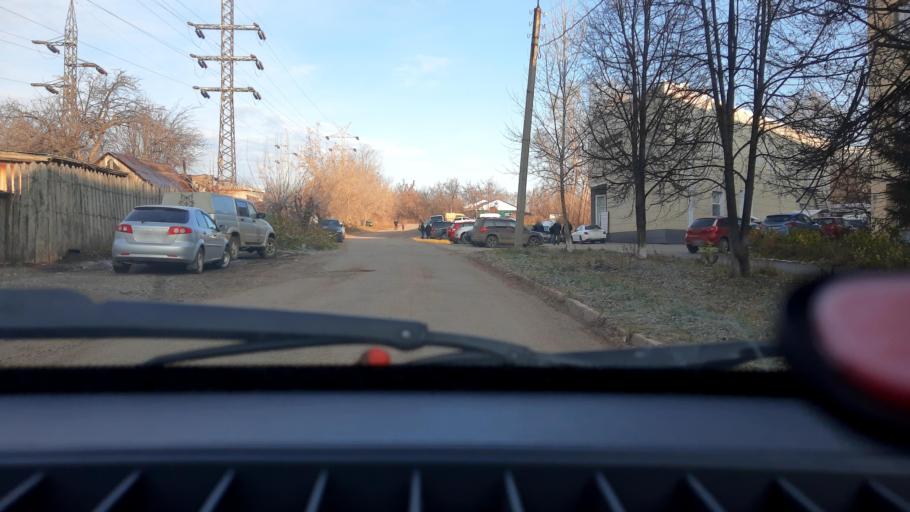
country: RU
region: Bashkortostan
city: Ufa
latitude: 54.8067
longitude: 56.0550
